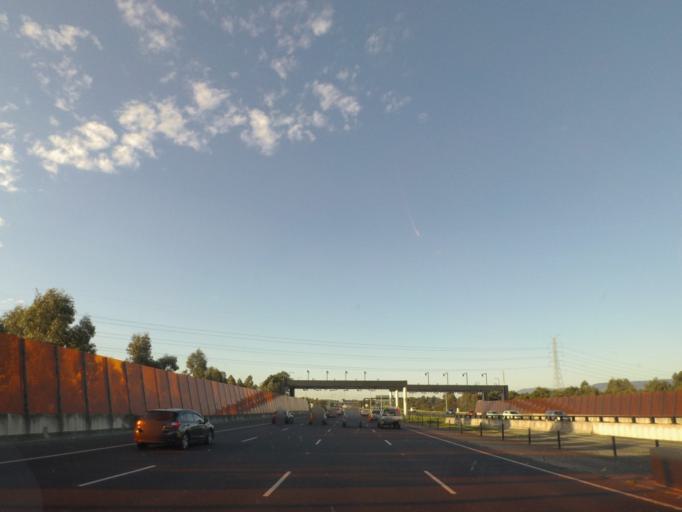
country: AU
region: Victoria
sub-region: Monash
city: Mulgrave
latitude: -37.9324
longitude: 145.2093
